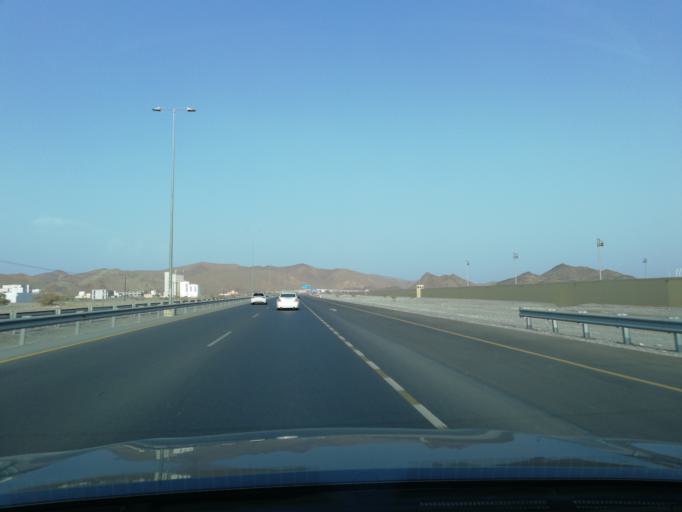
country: OM
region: Muhafazat ad Dakhiliyah
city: Izki
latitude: 22.8914
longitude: 57.6695
